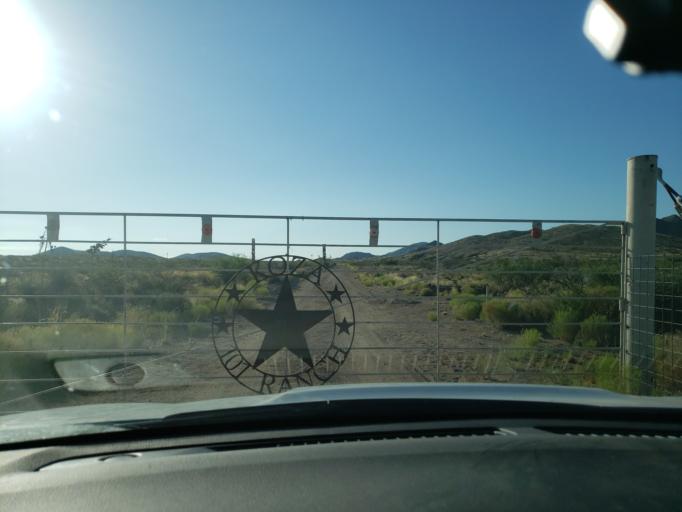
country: US
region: Texas
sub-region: Culberson County
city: Van Horn
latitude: 30.9338
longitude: -104.7251
